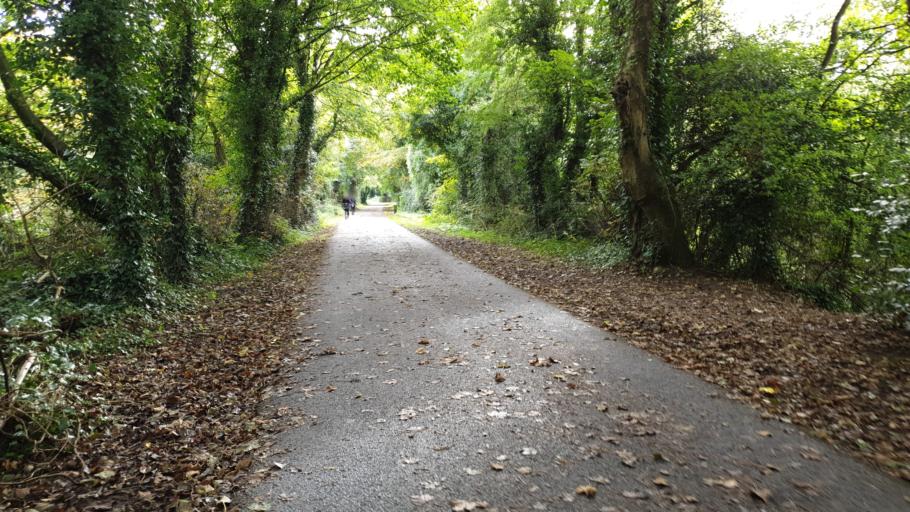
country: IE
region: Munster
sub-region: County Cork
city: Cork
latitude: 51.8986
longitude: -8.4235
